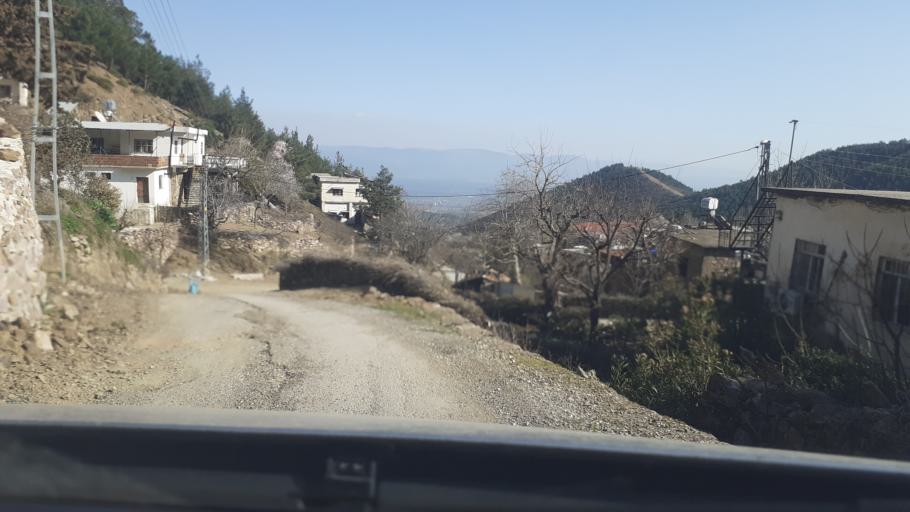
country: TR
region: Hatay
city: Aktepe
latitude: 36.7595
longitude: 36.4508
